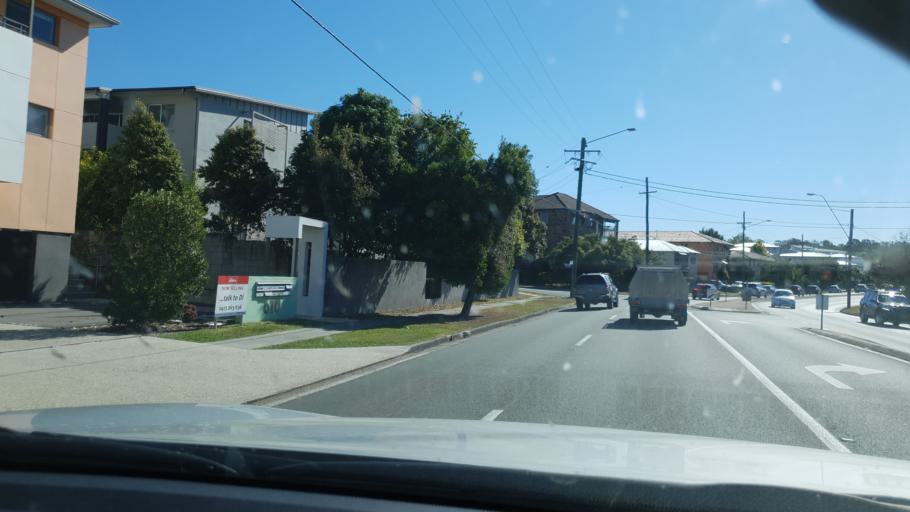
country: AU
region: Queensland
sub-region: Brisbane
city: Everton Park
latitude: -27.4051
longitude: 152.9892
